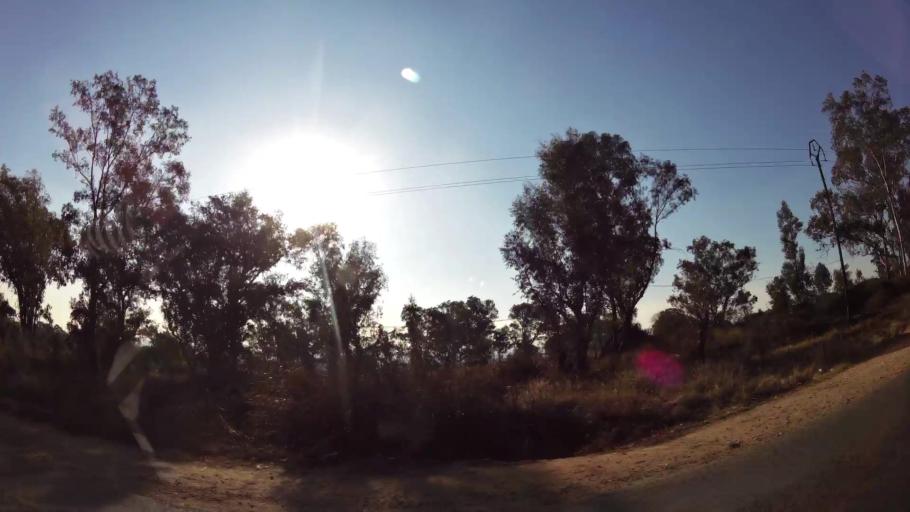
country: ZA
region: Gauteng
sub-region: West Rand District Municipality
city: Muldersdriseloop
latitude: -26.0199
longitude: 27.8803
